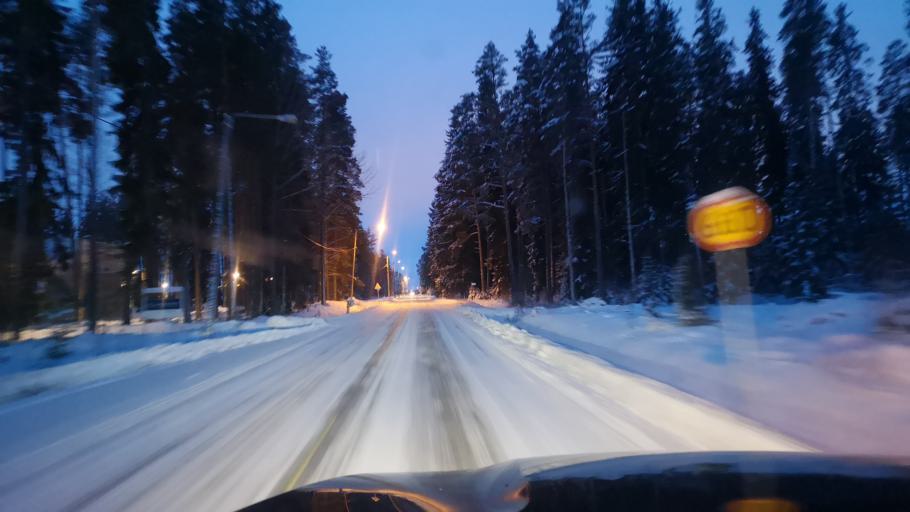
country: FI
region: Varsinais-Suomi
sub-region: Loimaa
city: Loimaa
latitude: 60.8685
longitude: 23.0878
